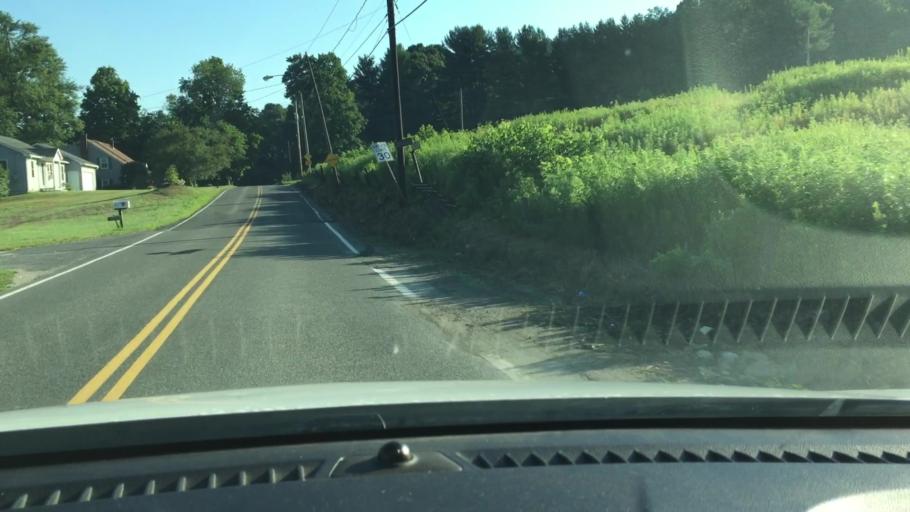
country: US
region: Massachusetts
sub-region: Berkshire County
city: Pittsfield
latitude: 42.4022
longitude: -73.2326
